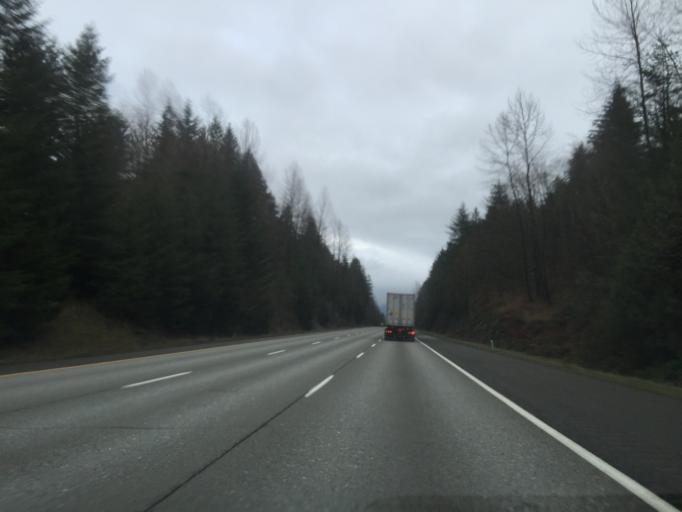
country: US
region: Washington
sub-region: King County
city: North Bend
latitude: 47.4941
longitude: -121.8107
